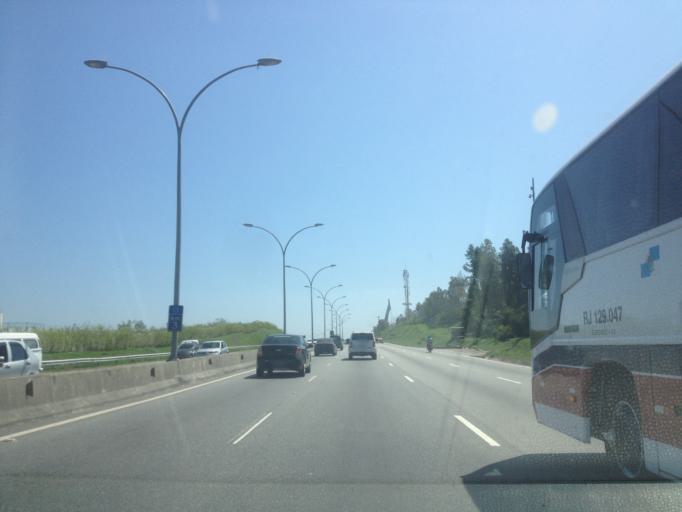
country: BR
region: Rio de Janeiro
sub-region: Rio De Janeiro
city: Rio de Janeiro
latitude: -22.8756
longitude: -43.2323
